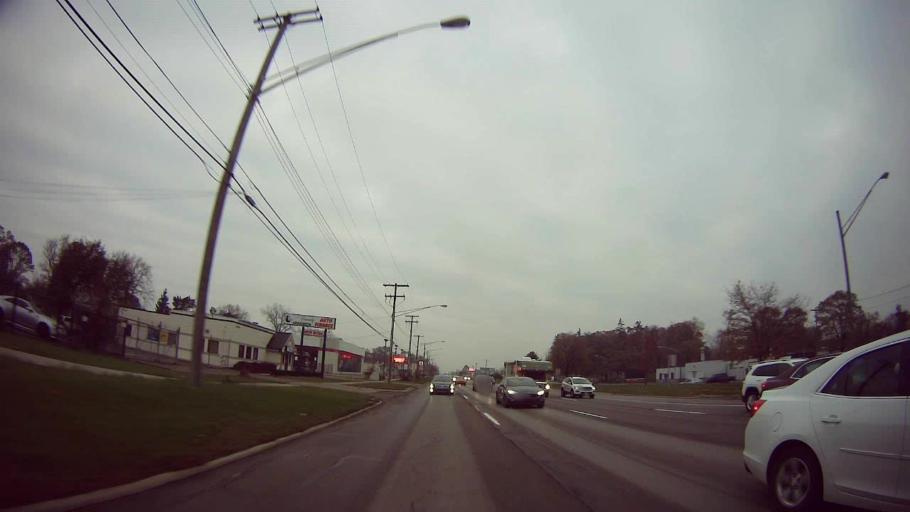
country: US
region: Michigan
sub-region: Wayne County
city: Redford
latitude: 42.4044
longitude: -83.2771
